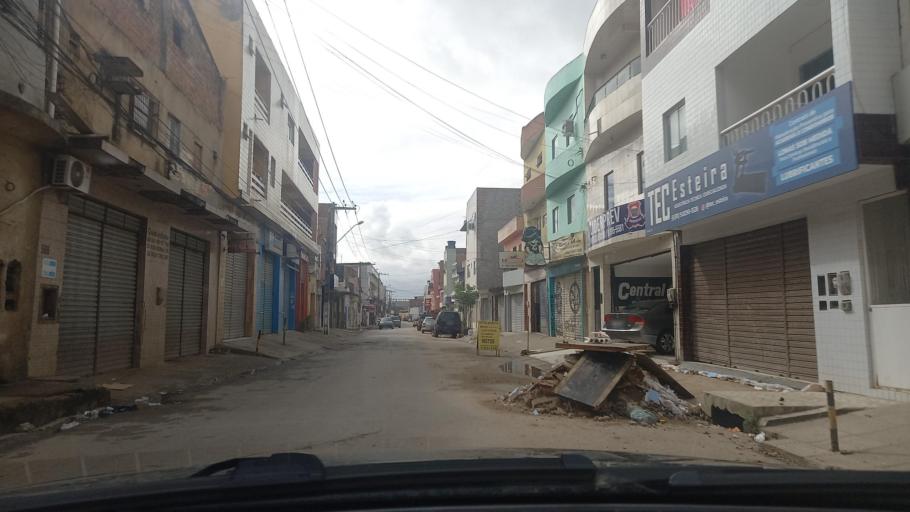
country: BR
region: Pernambuco
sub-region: Vitoria De Santo Antao
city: Vitoria de Santo Antao
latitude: -8.1181
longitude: -35.3026
